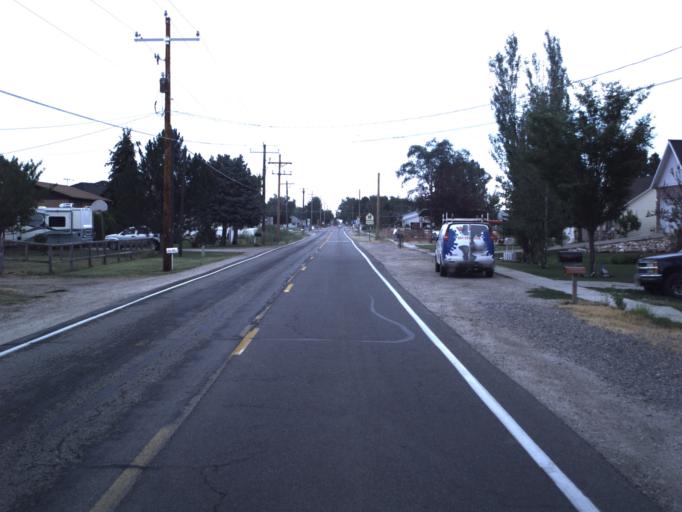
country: US
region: Utah
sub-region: Davis County
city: West Point
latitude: 41.1157
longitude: -112.1125
